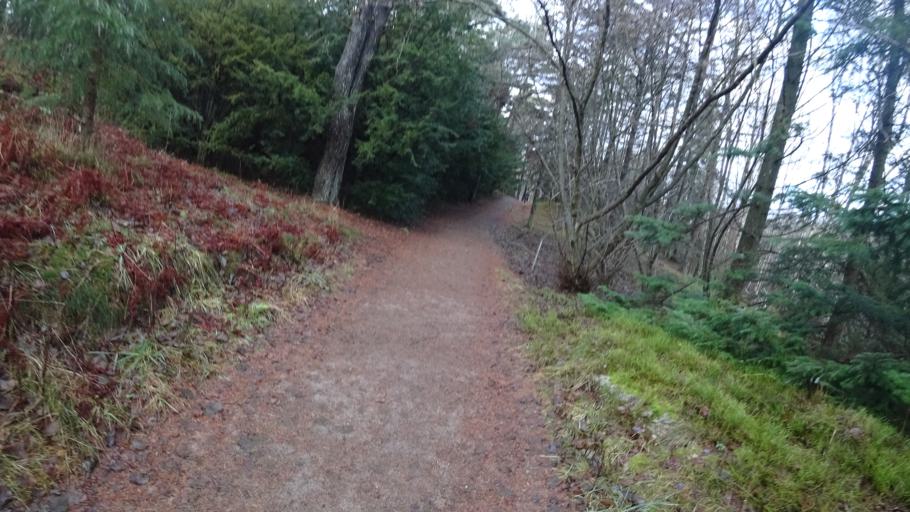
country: SE
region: Vaestra Goetaland
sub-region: Goteborg
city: Goeteborg
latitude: 57.6704
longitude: 11.9550
